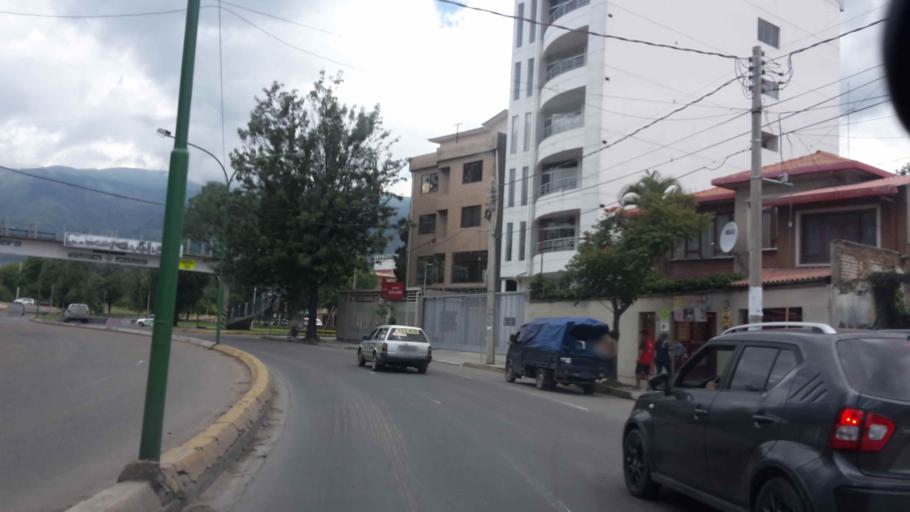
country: BO
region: Cochabamba
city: Cochabamba
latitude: -17.3903
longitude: -66.1638
